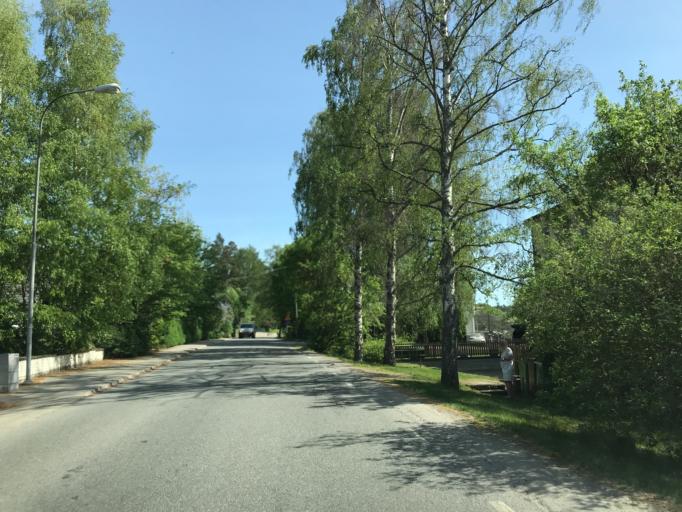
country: SE
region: Stockholm
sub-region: Sollentuna Kommun
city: Sollentuna
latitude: 59.4236
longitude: 17.9642
